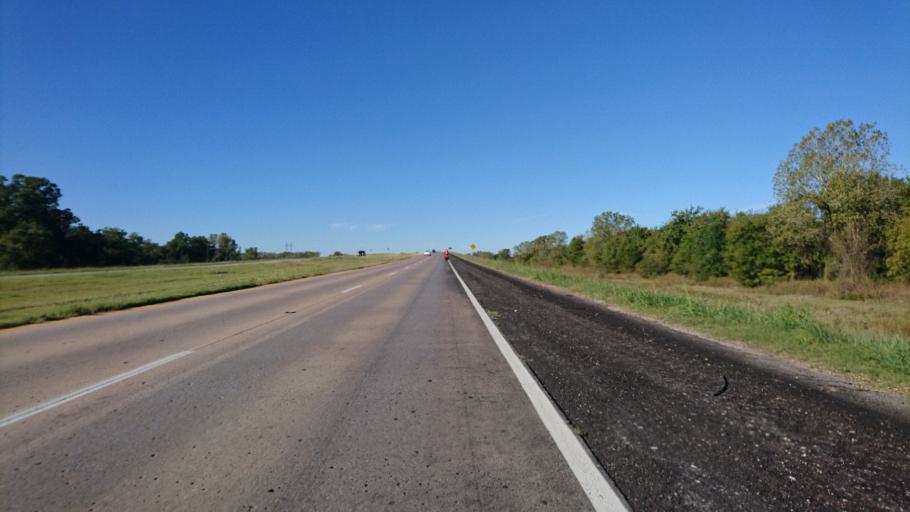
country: US
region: Oklahoma
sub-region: Rogers County
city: Verdigris
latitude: 36.2185
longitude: -95.7160
